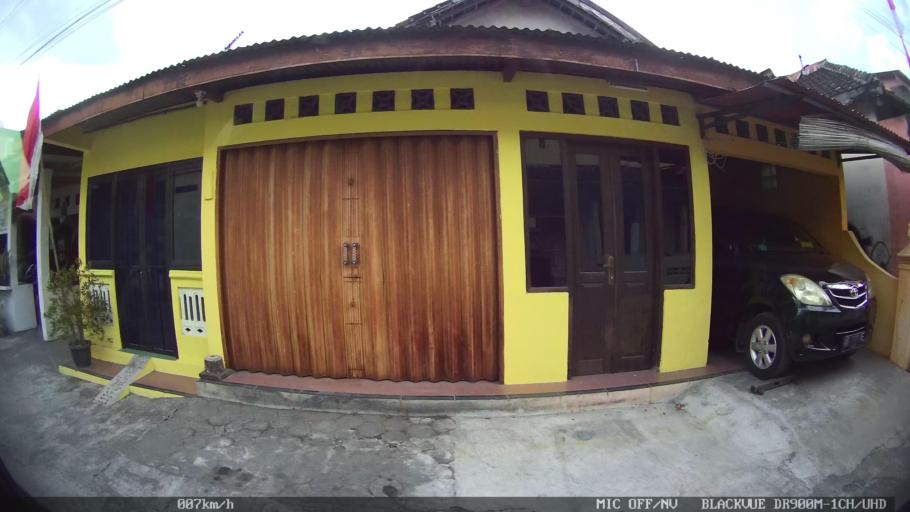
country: ID
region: Daerah Istimewa Yogyakarta
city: Kasihan
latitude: -7.8117
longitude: 110.3278
